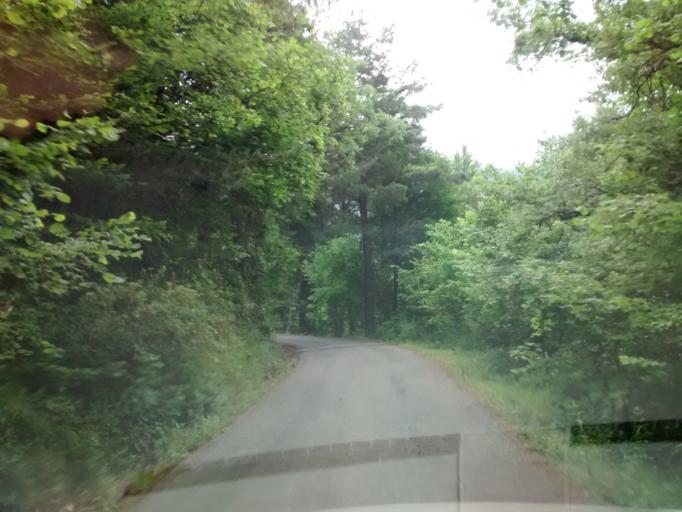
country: ES
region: Aragon
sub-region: Provincia de Huesca
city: Puertolas
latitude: 42.5861
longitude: 0.1341
